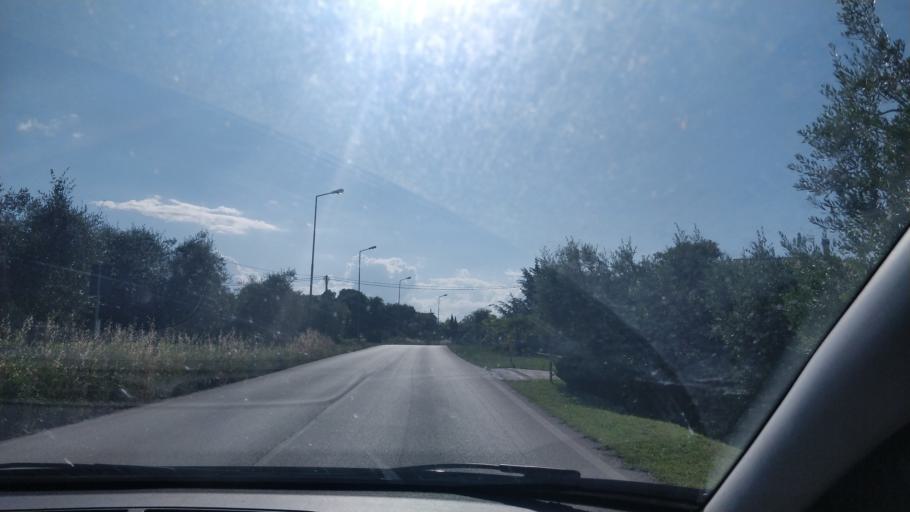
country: IT
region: The Marches
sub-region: Provincia di Ascoli Piceno
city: Cupra Marittima
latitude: 43.0355
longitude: 13.8390
